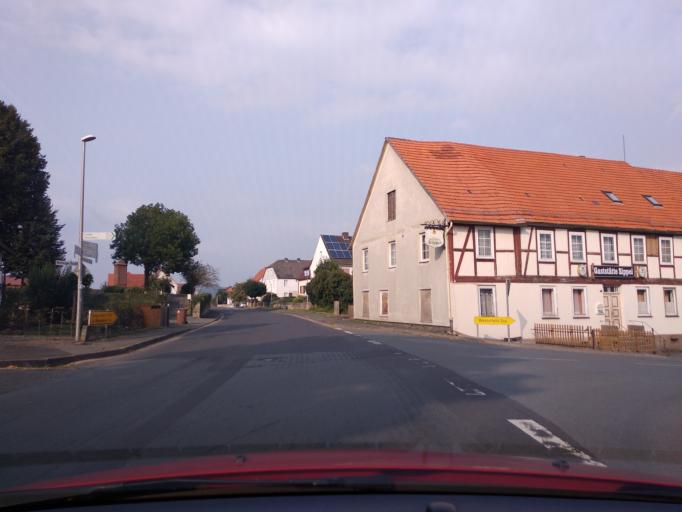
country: DE
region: Hesse
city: Liebenau
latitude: 51.4408
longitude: 9.3008
